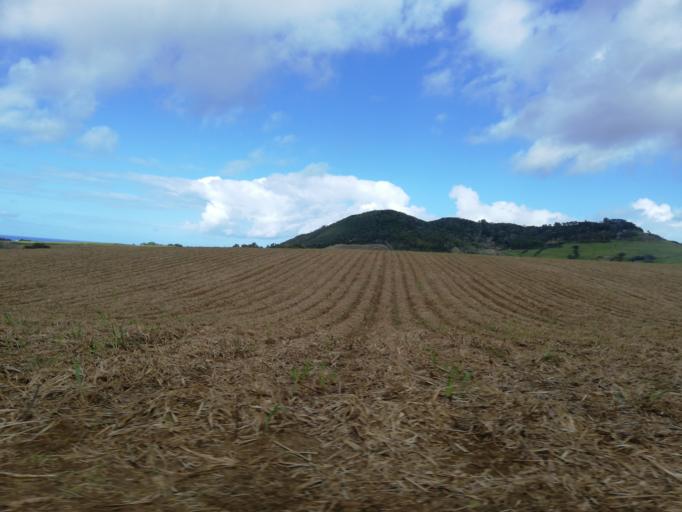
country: MU
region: Flacq
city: Grande Riviere Sud Est
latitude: -20.2795
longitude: 57.7586
